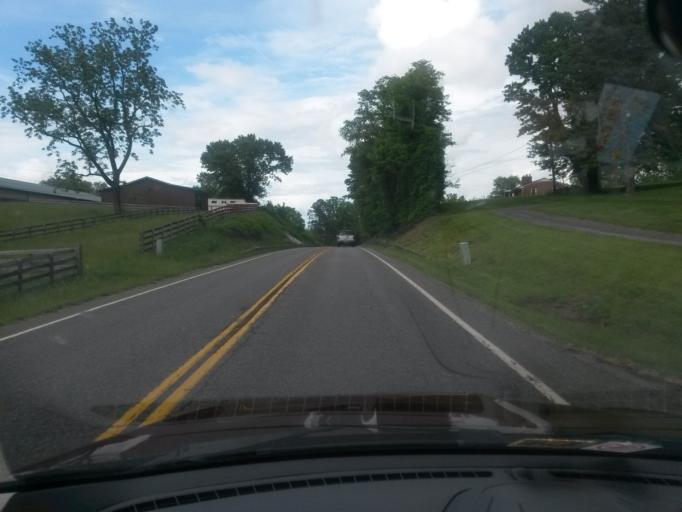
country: US
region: Virginia
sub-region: Montgomery County
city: Christiansburg
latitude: 37.1023
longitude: -80.4386
